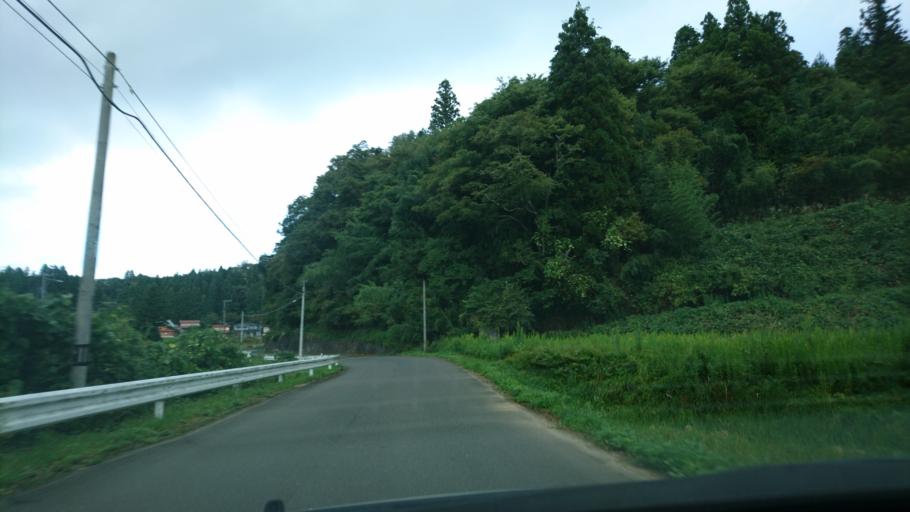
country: JP
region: Iwate
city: Ichinoseki
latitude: 38.9088
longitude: 141.0798
